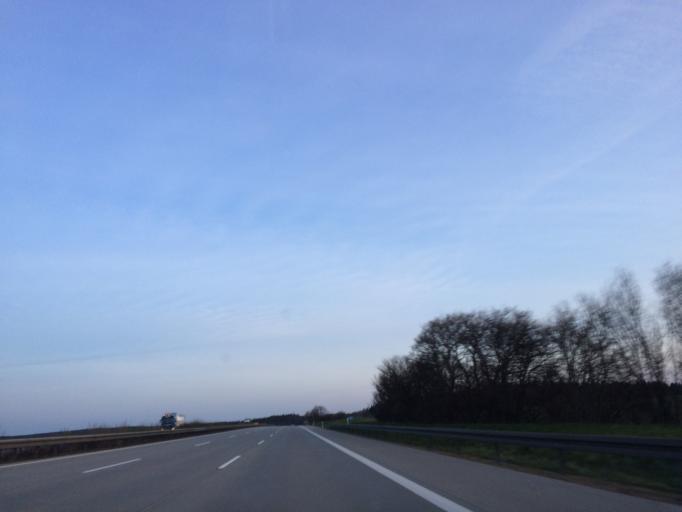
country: DE
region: Thuringia
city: Eineborn
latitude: 50.8336
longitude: 11.8751
